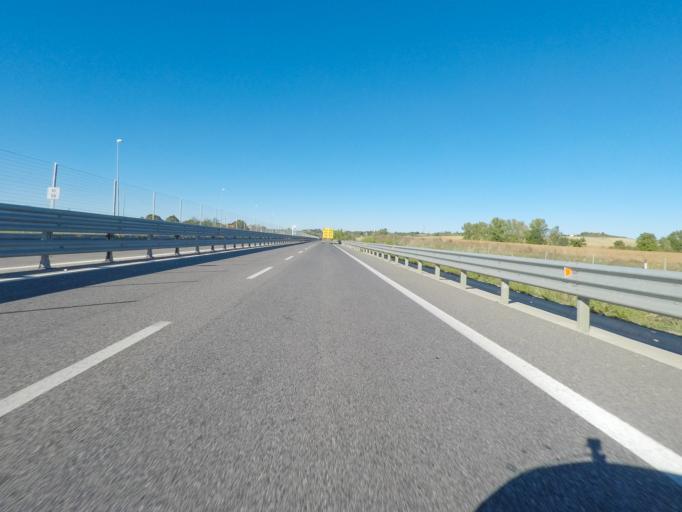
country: IT
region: Tuscany
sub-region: Provincia di Siena
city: Rosia
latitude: 43.2293
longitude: 11.2757
